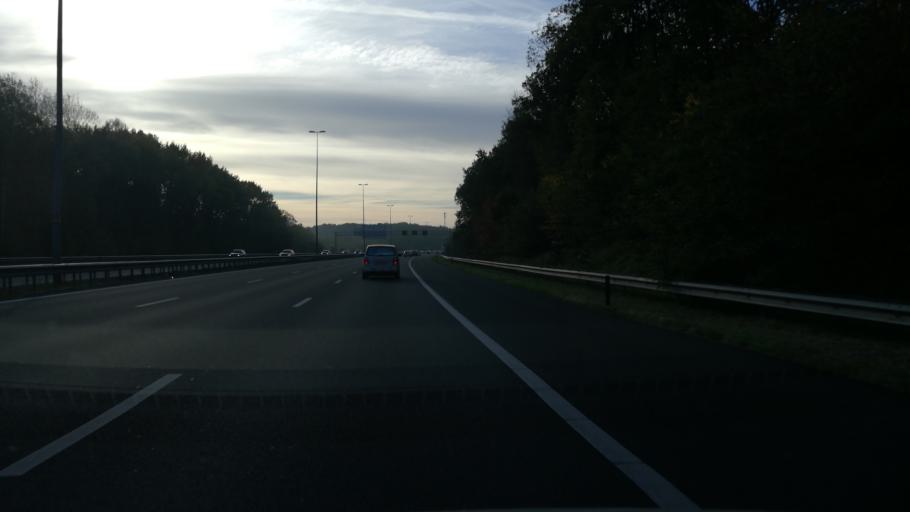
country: NL
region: Gelderland
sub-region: Gemeente Rozendaal
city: Rozendaal
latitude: 52.0074
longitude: 5.9461
